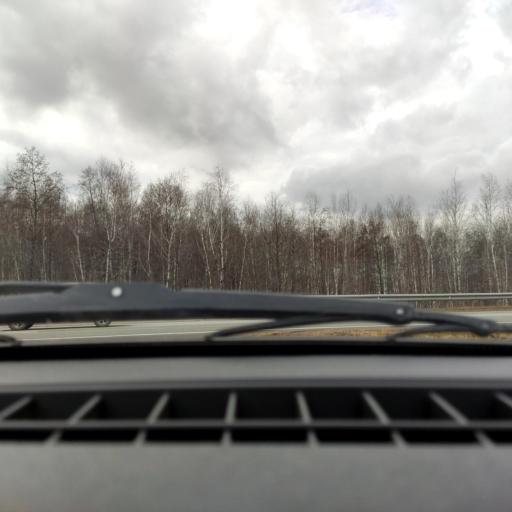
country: RU
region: Bashkortostan
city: Asanovo
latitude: 54.9666
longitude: 55.5819
